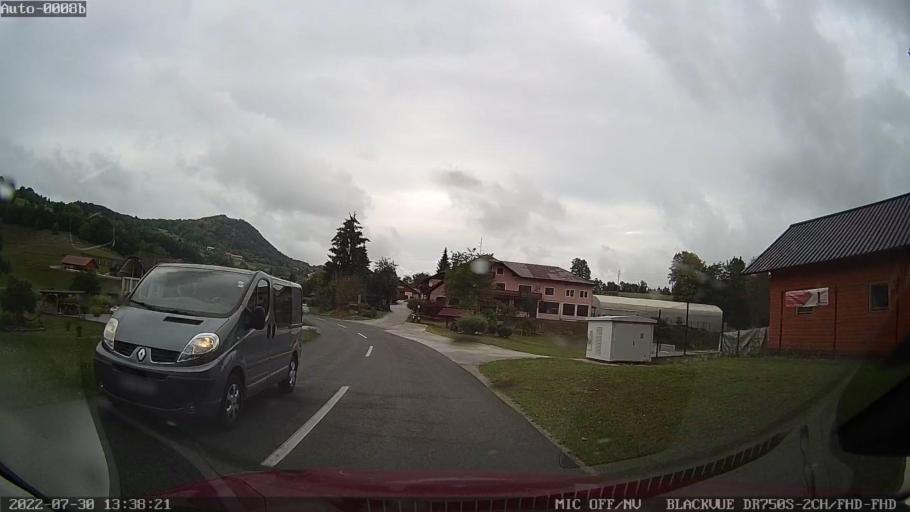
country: SI
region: Zuzemberk
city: Zuzemberk
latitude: 45.8835
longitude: 14.9107
